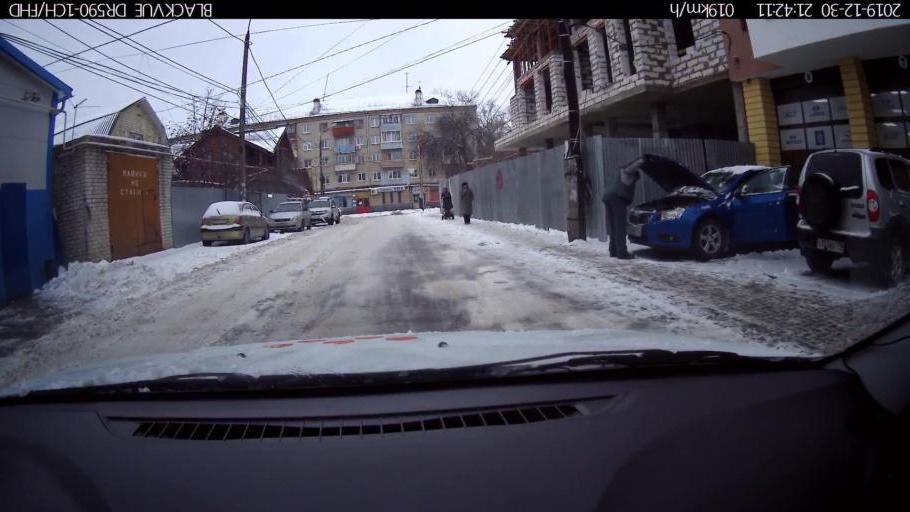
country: RU
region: Nizjnij Novgorod
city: Nizhniy Novgorod
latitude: 56.2736
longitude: 43.9253
